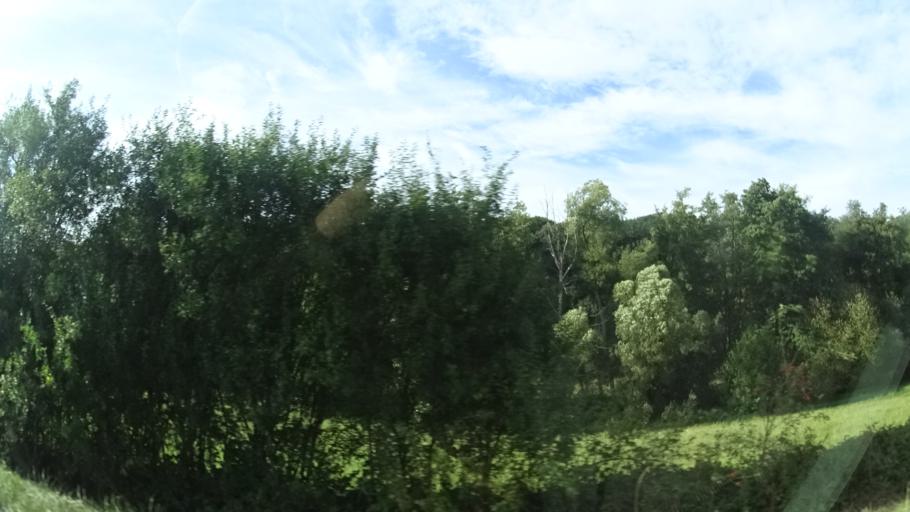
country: DE
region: Hesse
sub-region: Regierungsbezirk Kassel
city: Eichenzell
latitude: 50.5158
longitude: 9.6929
